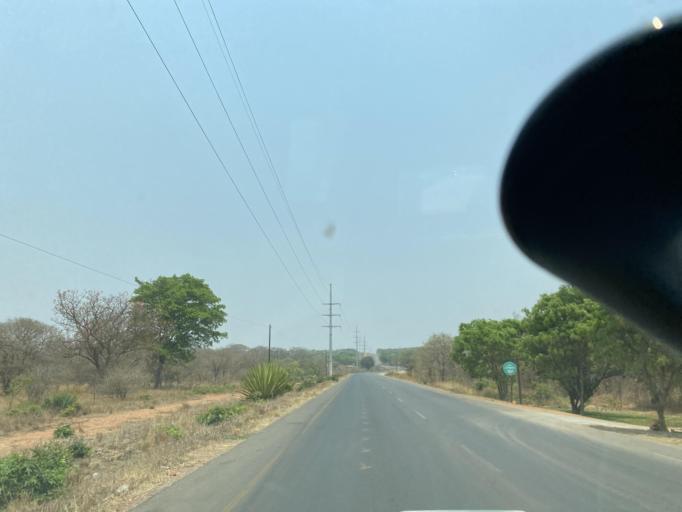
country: ZM
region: Lusaka
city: Lusaka
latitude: -15.5242
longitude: 28.4611
